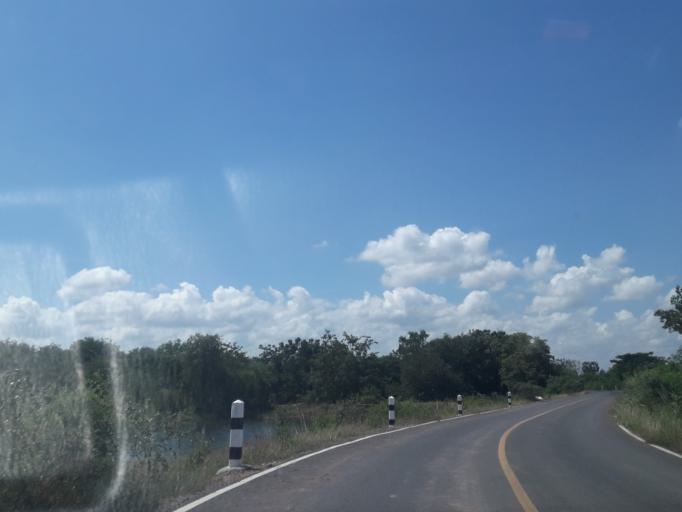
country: TH
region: Lop Buri
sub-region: Amphoe Tha Luang
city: Tha Luang
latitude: 15.0506
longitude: 101.0162
